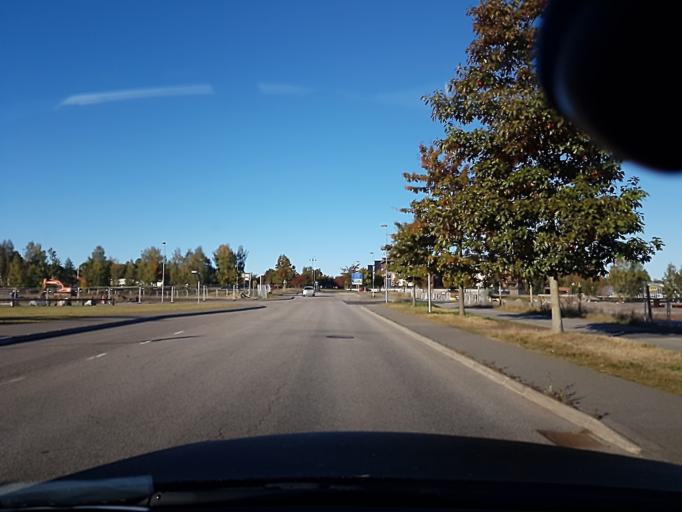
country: SE
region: Kronoberg
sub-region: Vaxjo Kommun
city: Vaexjoe
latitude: 56.8584
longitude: 14.8244
